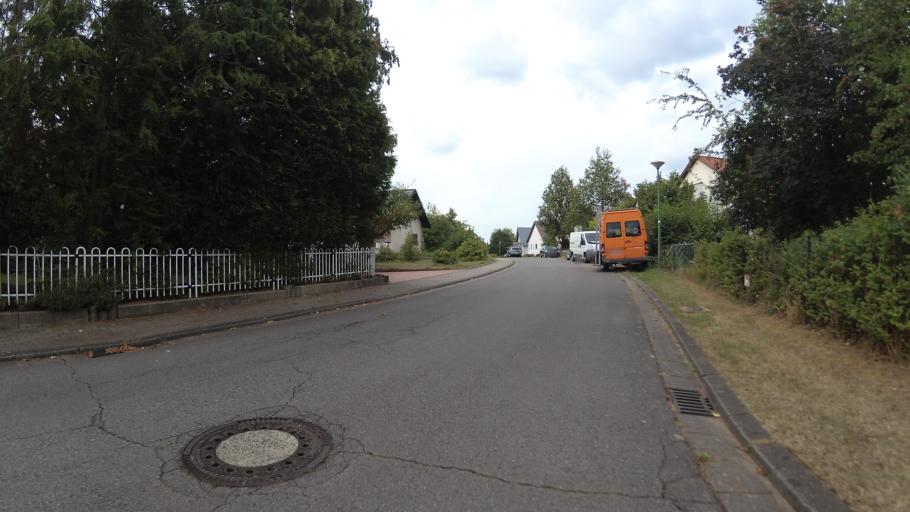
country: DE
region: Saarland
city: Bexbach
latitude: 49.3049
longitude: 7.2755
